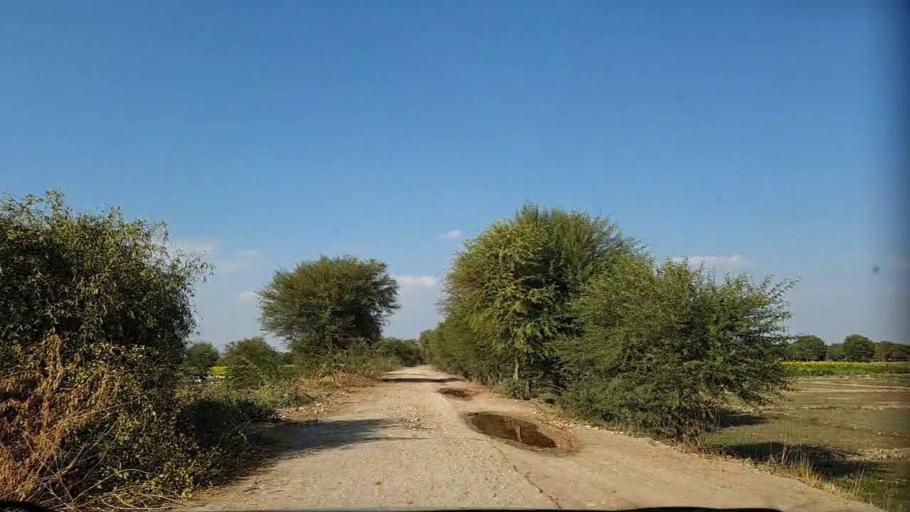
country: PK
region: Sindh
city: Pithoro
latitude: 25.6295
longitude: 69.3518
